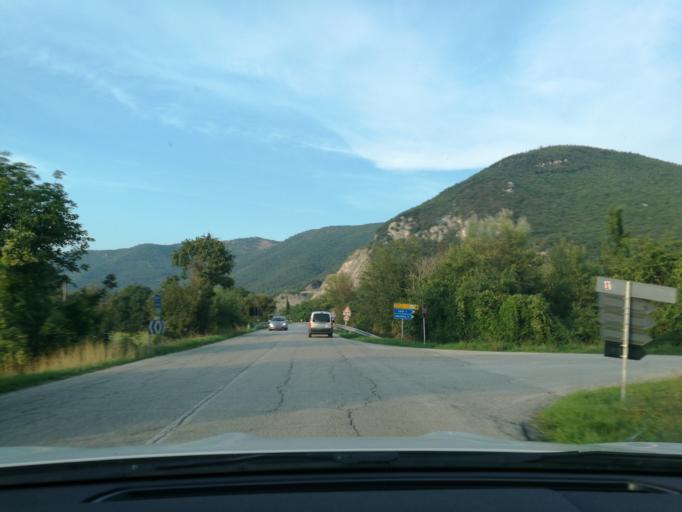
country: IT
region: Umbria
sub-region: Provincia di Terni
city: Acquasparta
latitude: 42.6669
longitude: 12.5502
